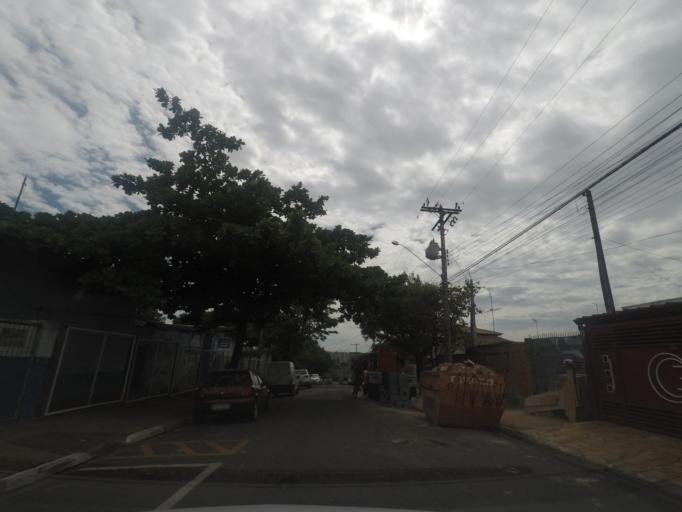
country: BR
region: Sao Paulo
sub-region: Sumare
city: Sumare
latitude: -22.8001
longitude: -47.2781
